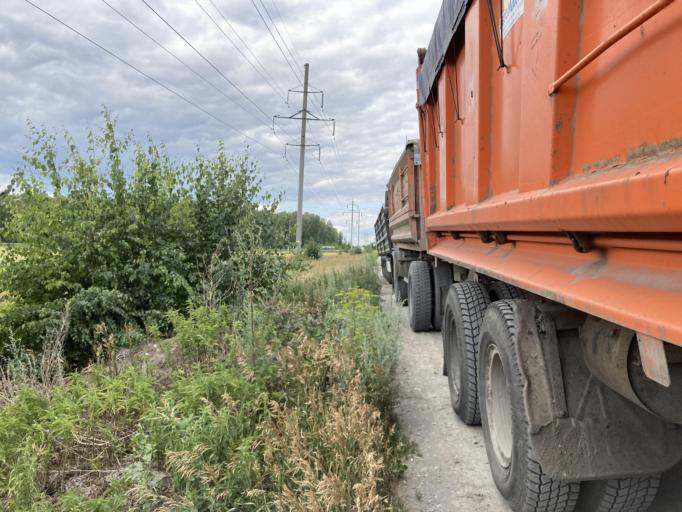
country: RU
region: Sverdlovsk
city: Bogdanovich
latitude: 56.8053
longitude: 62.0349
